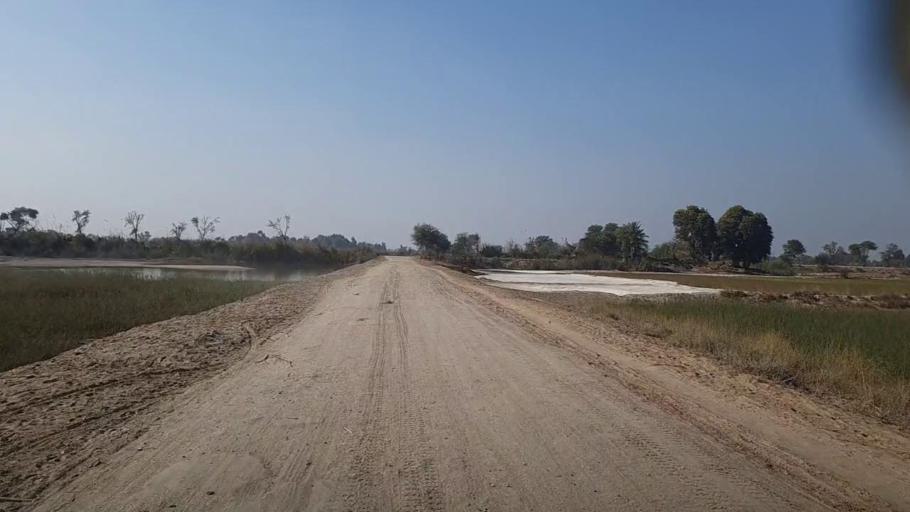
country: PK
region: Sindh
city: Mirpur Mathelo
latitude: 27.8992
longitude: 69.6453
